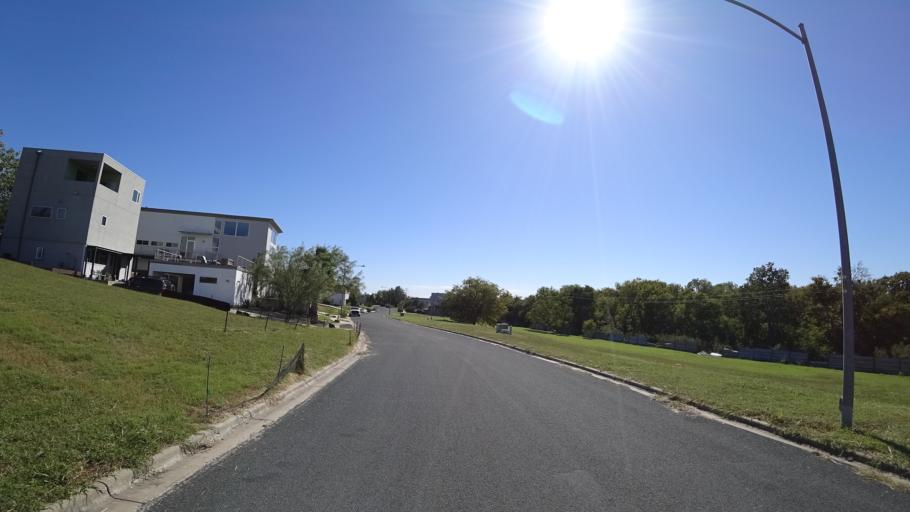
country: US
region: Texas
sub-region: Travis County
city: Hornsby Bend
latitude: 30.2846
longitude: -97.6483
